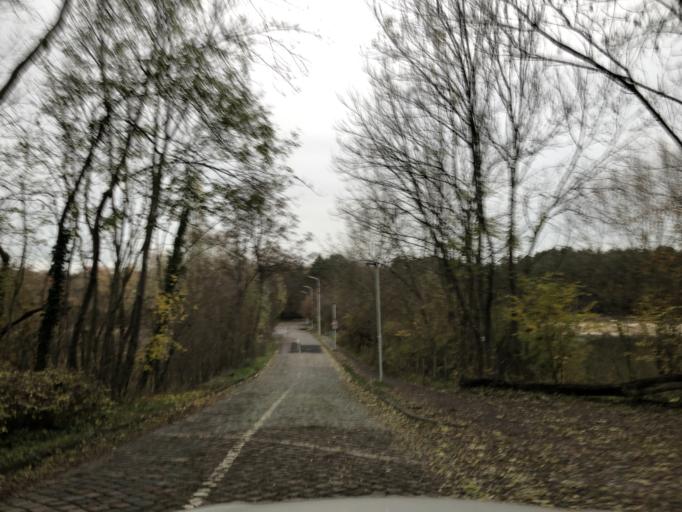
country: DE
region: Saxony-Anhalt
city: Halle Neustadt
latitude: 51.4829
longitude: 11.8911
